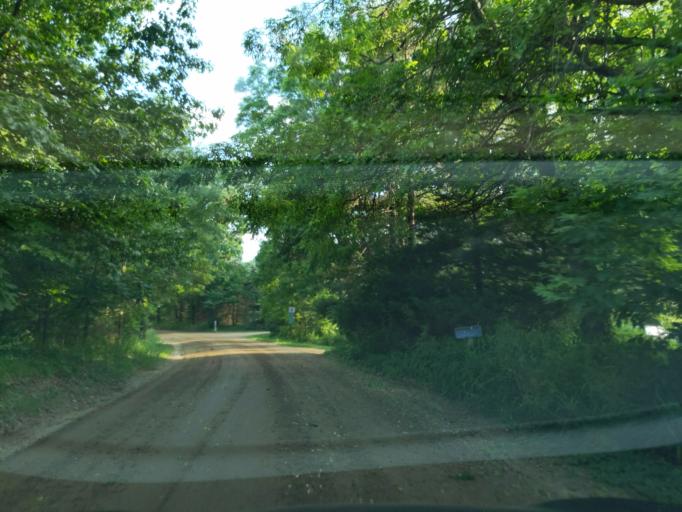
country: US
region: Michigan
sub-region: Shiawassee County
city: Laingsburg
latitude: 42.8536
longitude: -84.3642
